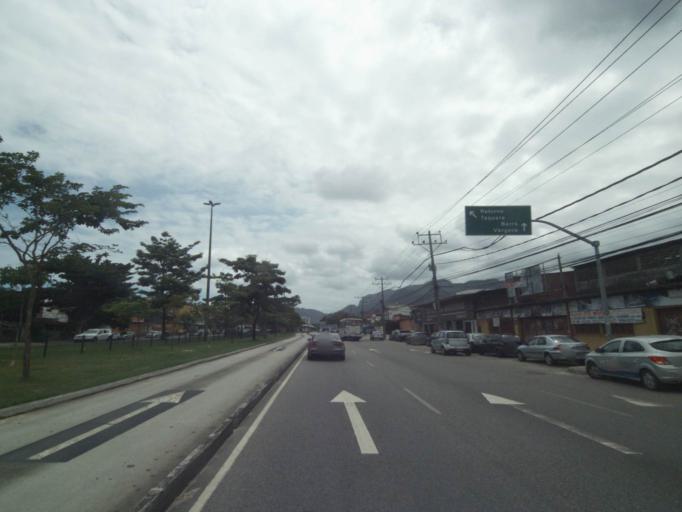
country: BR
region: Rio de Janeiro
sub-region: Nilopolis
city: Nilopolis
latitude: -22.9590
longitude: -43.3853
